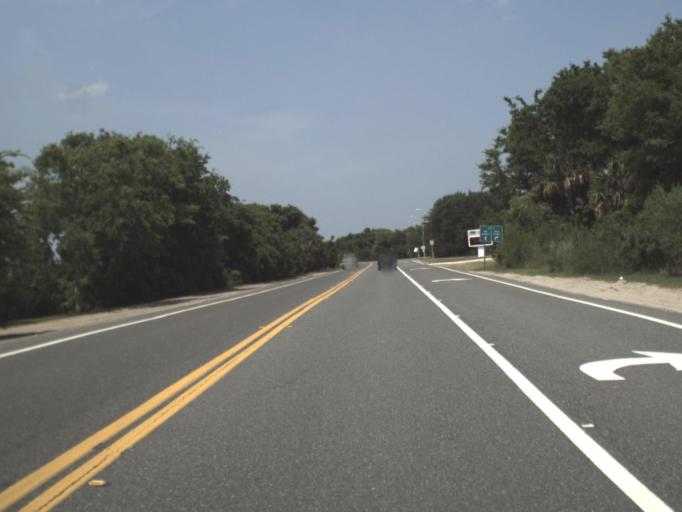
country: US
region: Florida
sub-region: Duval County
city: Atlantic Beach
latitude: 30.3831
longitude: -81.4374
